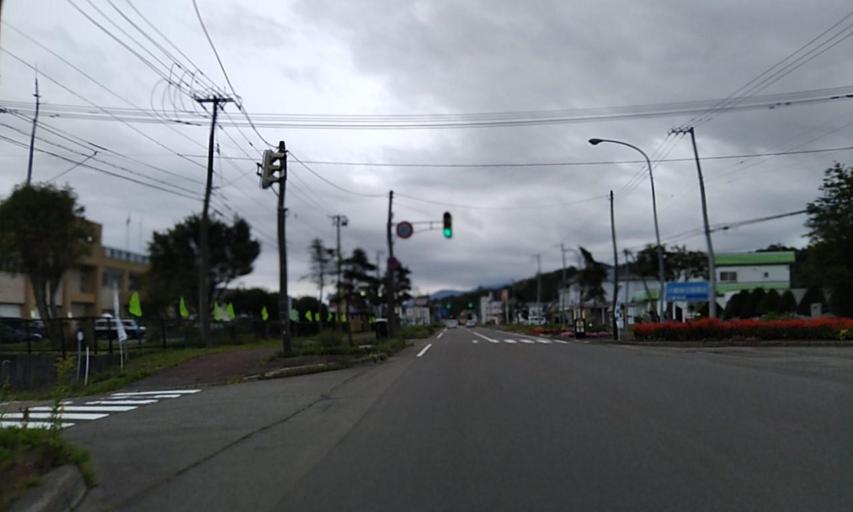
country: JP
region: Hokkaido
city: Obihiro
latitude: 42.2962
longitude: 143.3135
